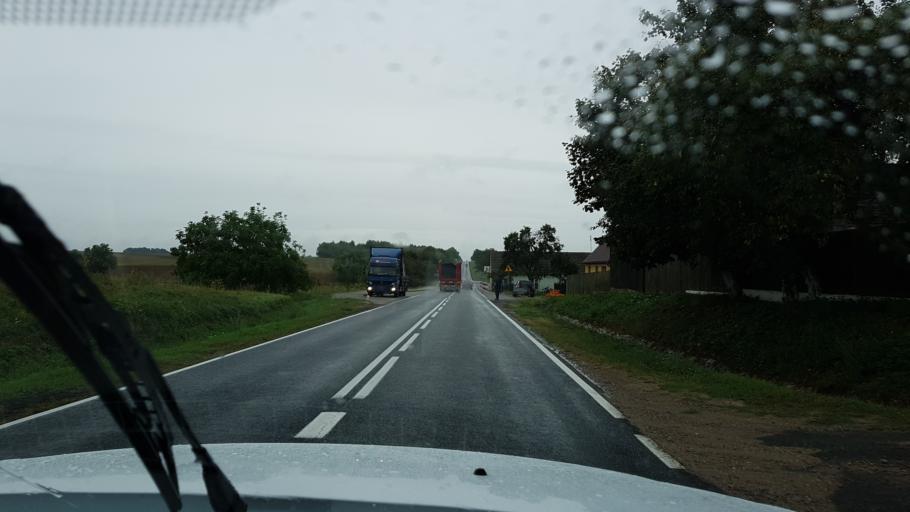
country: DE
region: Brandenburg
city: Schwedt (Oder)
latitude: 53.0272
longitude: 14.3221
